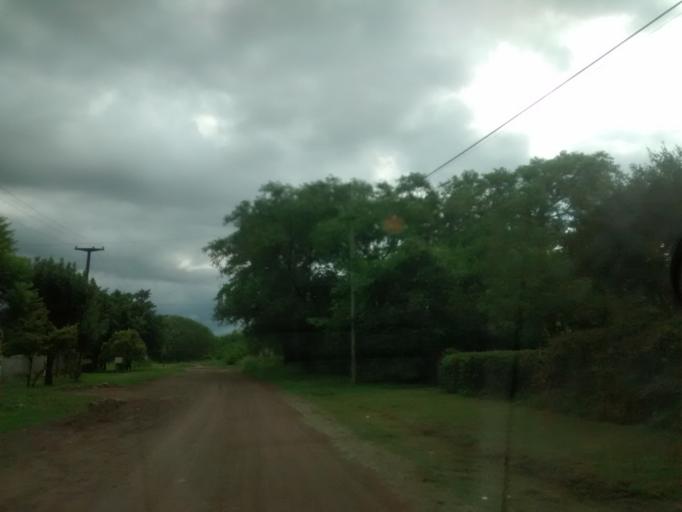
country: AR
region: Chaco
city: Puerto Tirol
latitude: -27.3804
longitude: -59.0898
